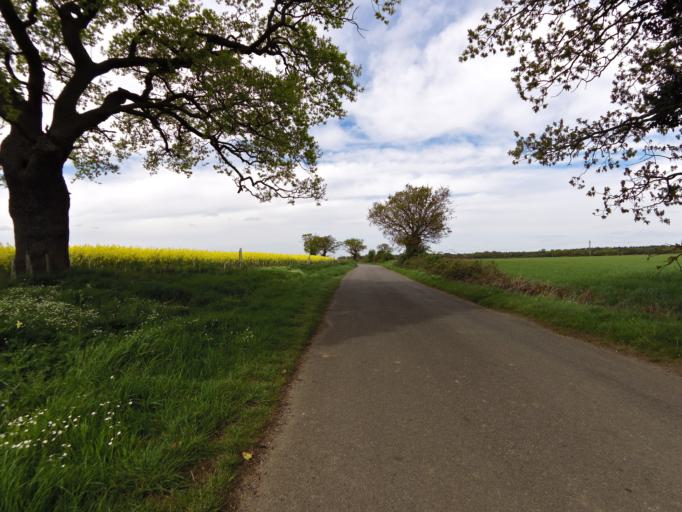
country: GB
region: England
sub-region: Essex
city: Mistley
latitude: 51.9932
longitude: 1.1309
